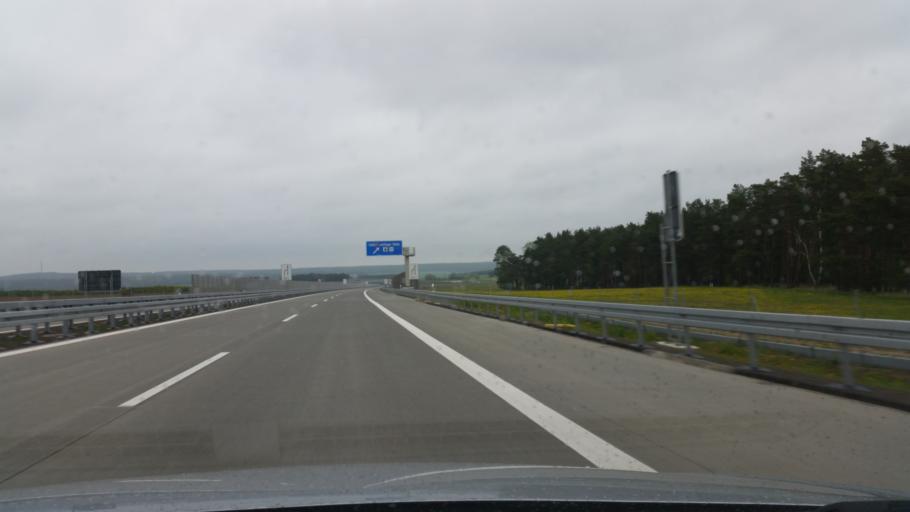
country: DE
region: Saxony-Anhalt
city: Burgstall
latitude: 52.3946
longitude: 11.6295
